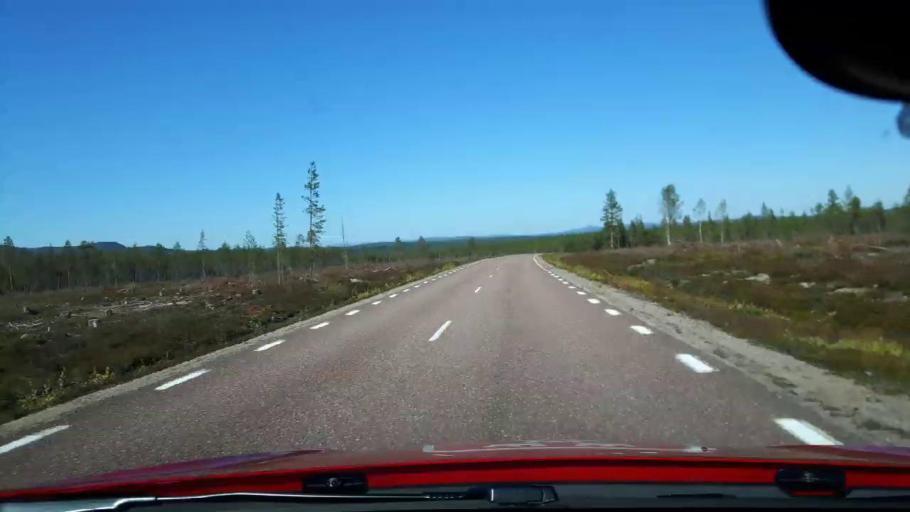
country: SE
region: Jaemtland
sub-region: Harjedalens Kommun
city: Sveg
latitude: 61.7441
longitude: 14.1589
